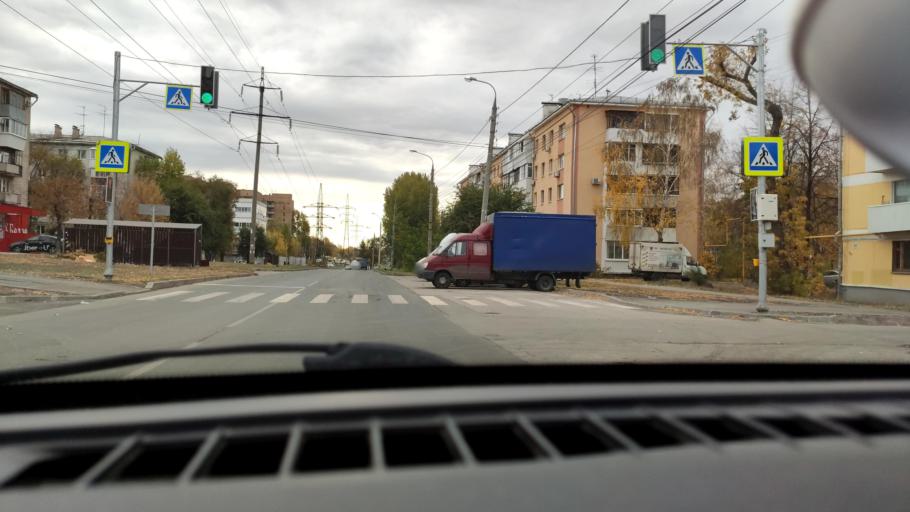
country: RU
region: Samara
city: Samara
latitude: 53.1937
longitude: 50.1717
